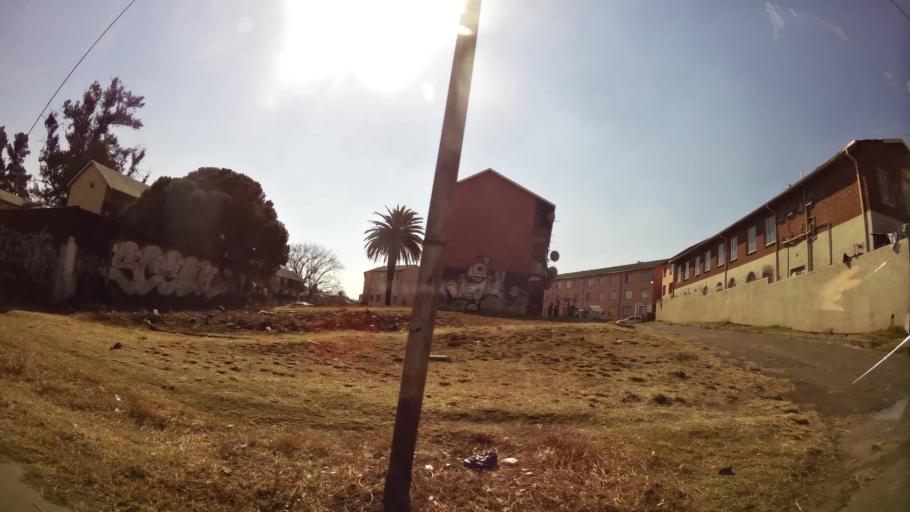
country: ZA
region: Gauteng
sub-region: City of Johannesburg Metropolitan Municipality
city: Johannesburg
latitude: -26.1866
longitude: 27.9653
